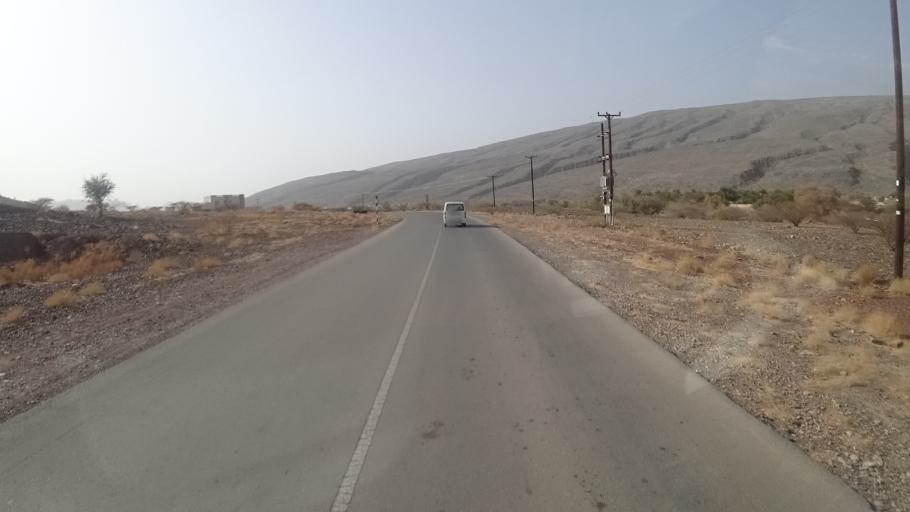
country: OM
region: Muhafazat ad Dakhiliyah
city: Bahla'
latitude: 23.0545
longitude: 57.4188
